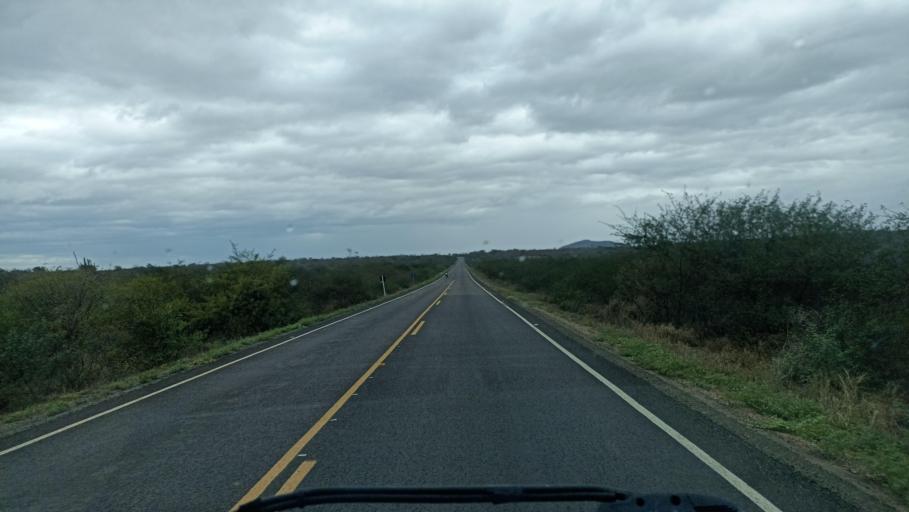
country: BR
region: Bahia
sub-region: Iacu
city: Iacu
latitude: -12.9730
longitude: -40.5054
